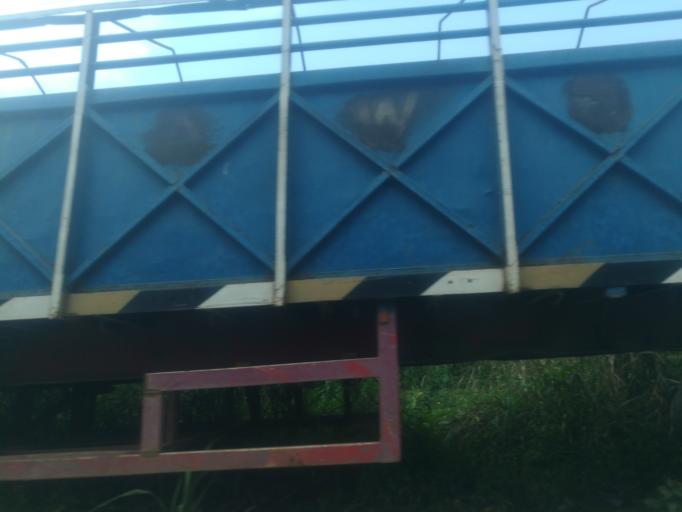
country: NG
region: Oyo
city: Ibadan
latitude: 7.3684
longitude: 3.8569
